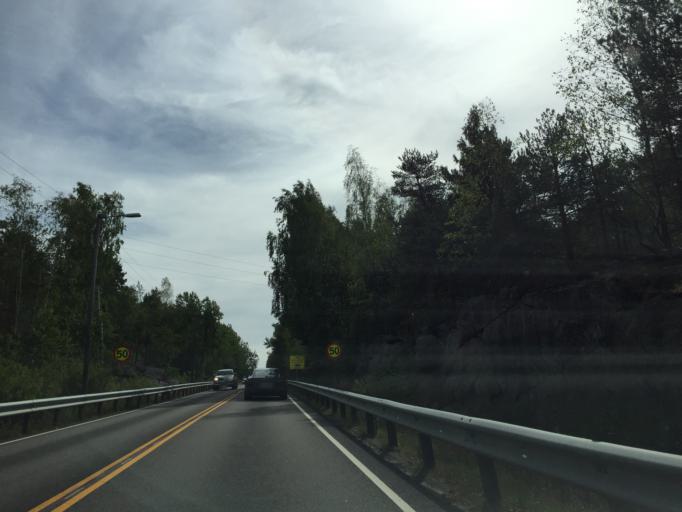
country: NO
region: Ostfold
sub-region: Fredrikstad
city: Fredrikstad
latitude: 59.1532
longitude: 10.9365
